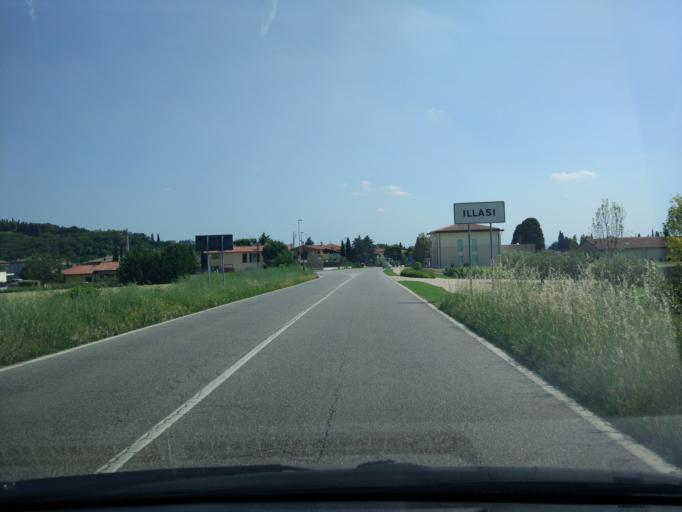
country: IT
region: Veneto
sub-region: Provincia di Verona
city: Cellore
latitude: 45.4773
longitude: 11.1808
